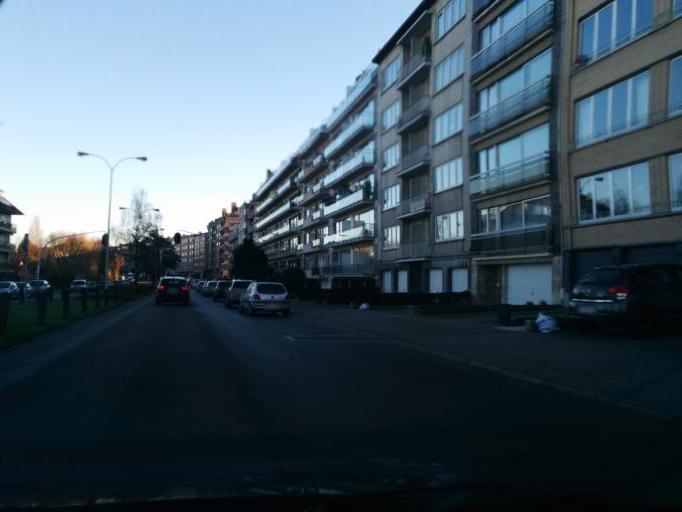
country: BE
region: Flanders
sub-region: Provincie Vlaams-Brabant
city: Wemmel
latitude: 50.8720
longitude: 4.3032
